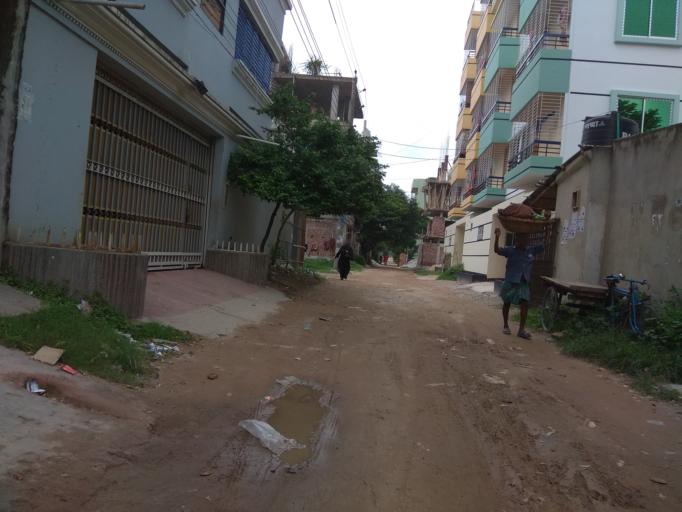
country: BD
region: Dhaka
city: Tungi
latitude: 23.8281
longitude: 90.3497
